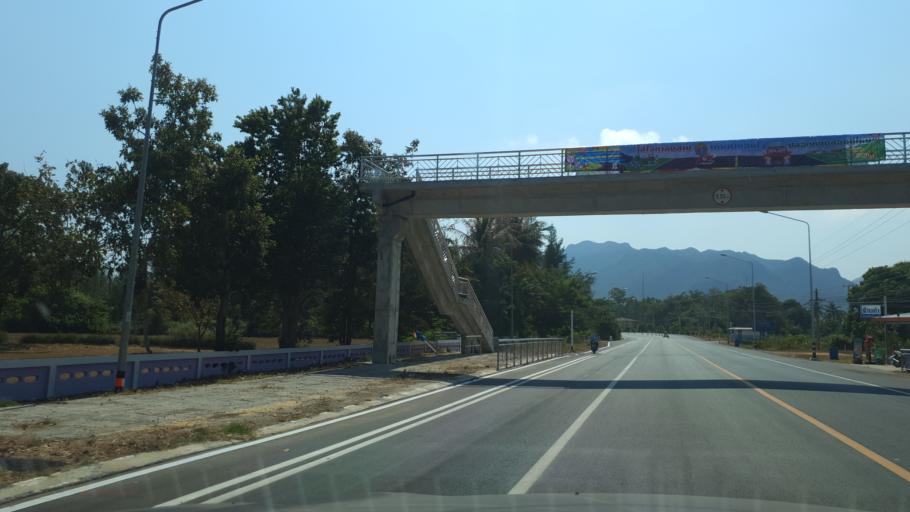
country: TH
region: Prachuap Khiri Khan
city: Sam Roi Yot
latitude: 12.2490
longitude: 99.9638
